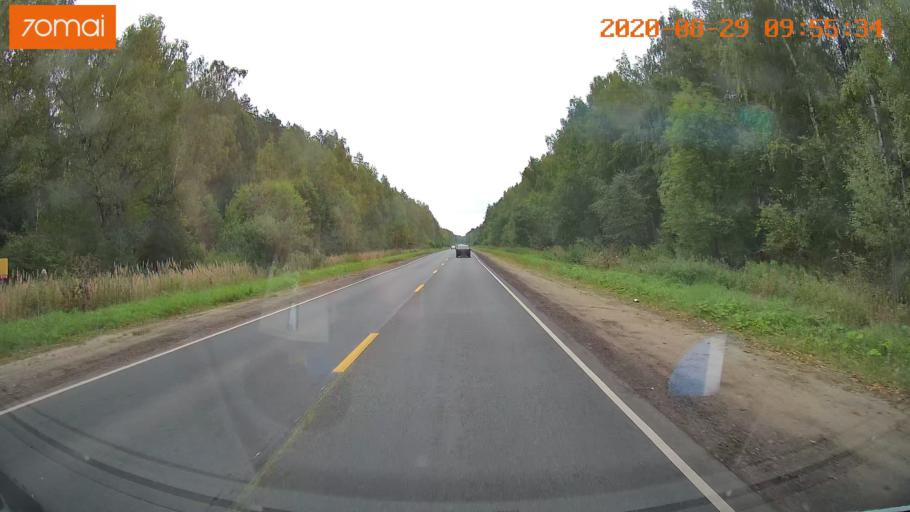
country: RU
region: Ivanovo
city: Zarechnyy
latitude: 57.4221
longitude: 42.2668
